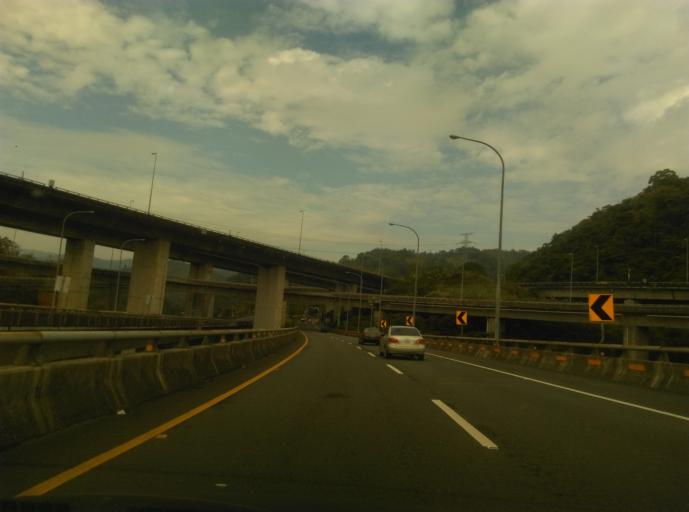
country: TW
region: Taiwan
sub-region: Keelung
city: Keelung
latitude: 25.1253
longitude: 121.6985
